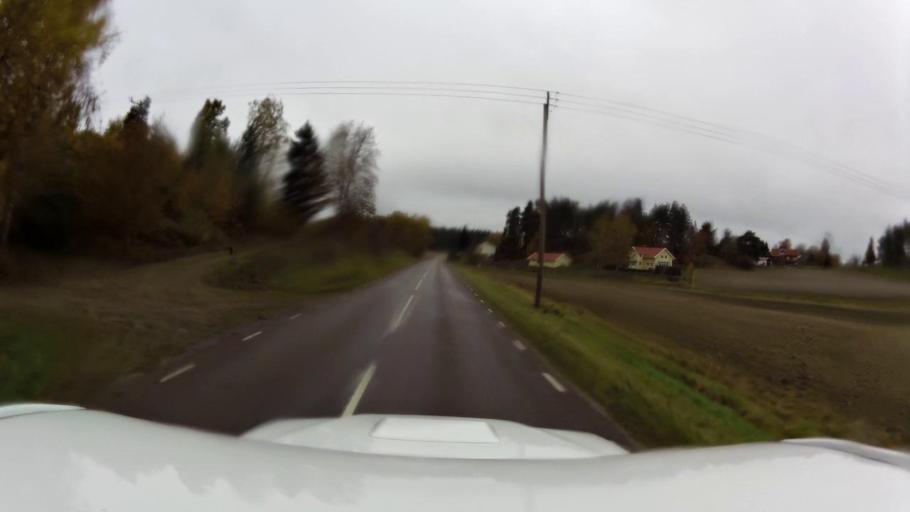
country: SE
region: OEstergoetland
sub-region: Norrkopings Kommun
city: Kimstad
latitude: 58.4154
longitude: 15.9196
